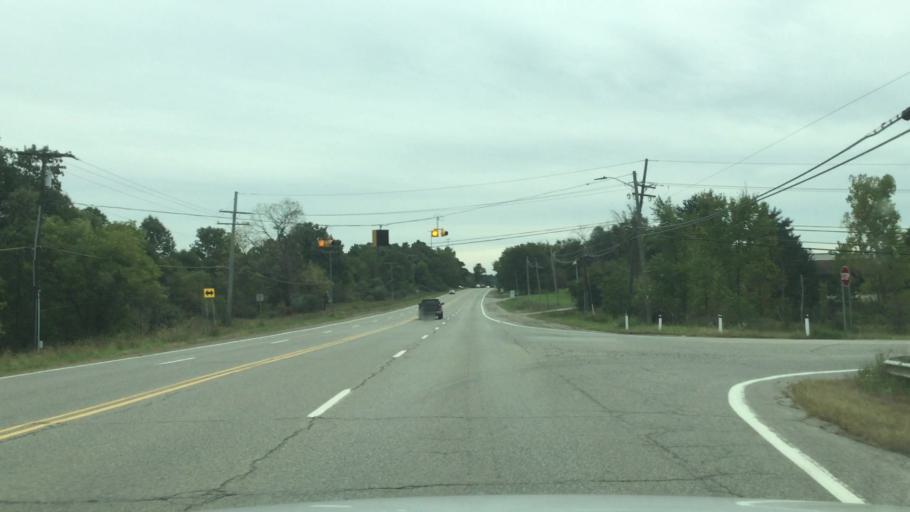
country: US
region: Michigan
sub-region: Oakland County
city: Ortonville
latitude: 42.7808
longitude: -83.4995
